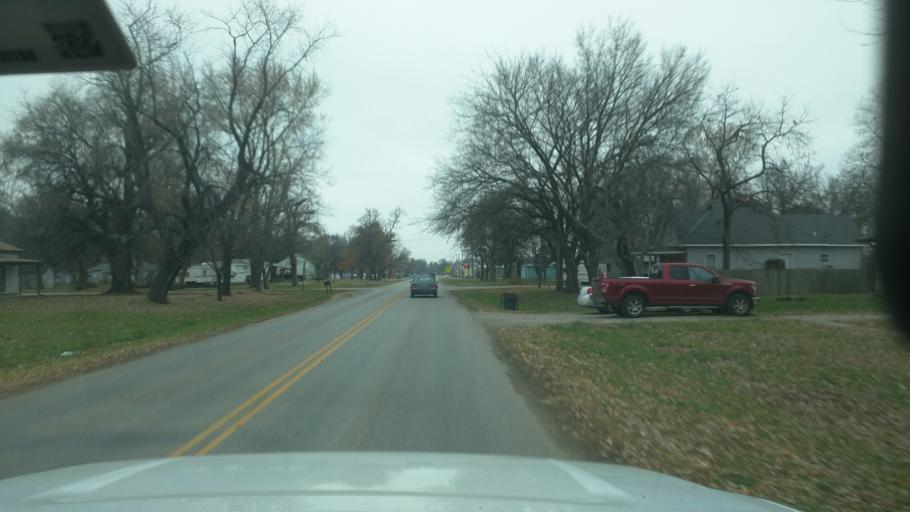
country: US
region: Kansas
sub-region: Lyon County
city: Emporia
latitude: 38.5098
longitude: -96.2621
